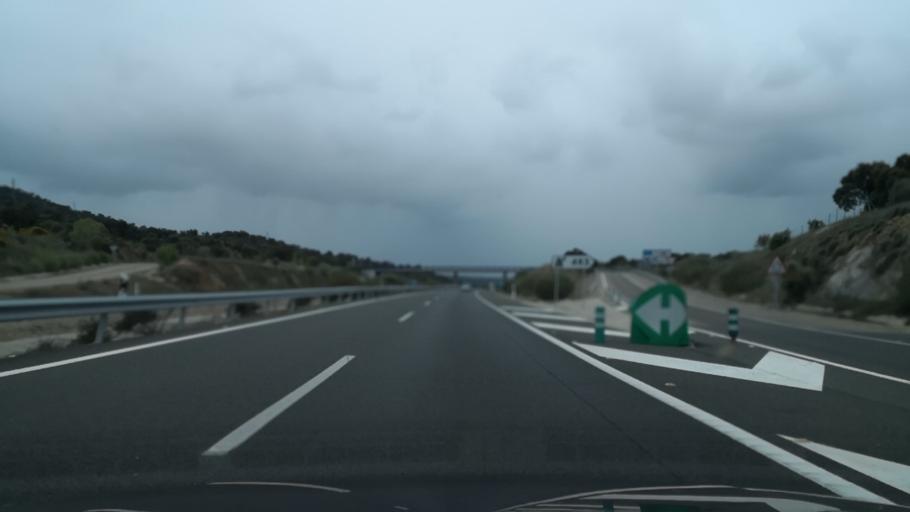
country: ES
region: Extremadura
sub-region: Provincia de Caceres
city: Oliva de Plasencia
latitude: 40.0851
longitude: -6.0783
